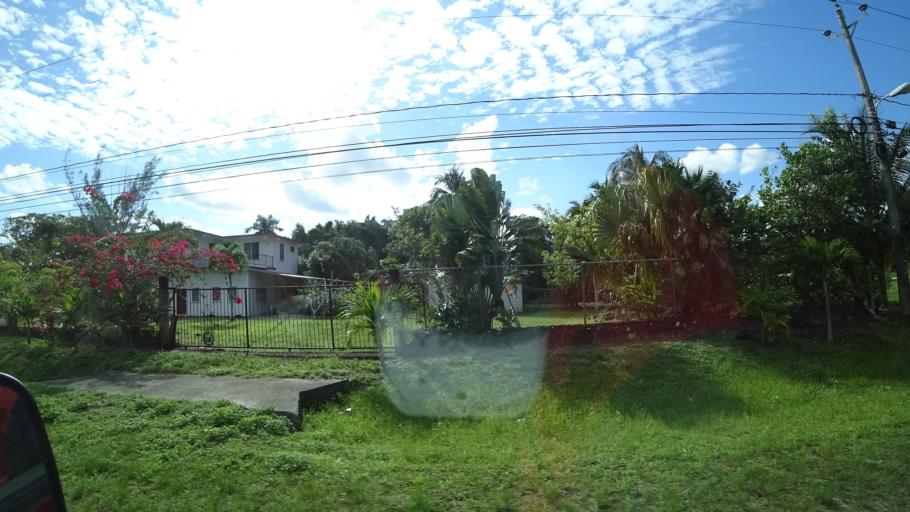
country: BZ
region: Belize
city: Belize City
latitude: 17.5636
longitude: -88.4058
